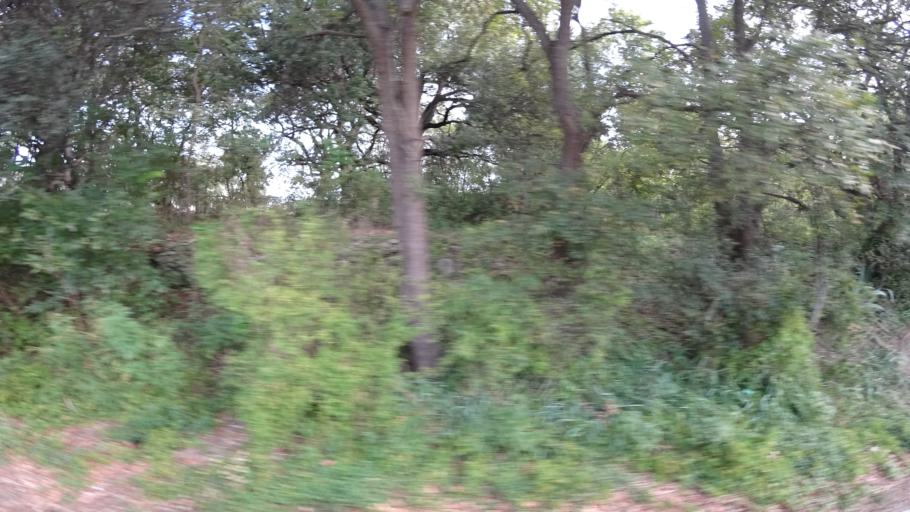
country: US
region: Texas
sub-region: Travis County
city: Austin
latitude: 30.2058
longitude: -97.7381
